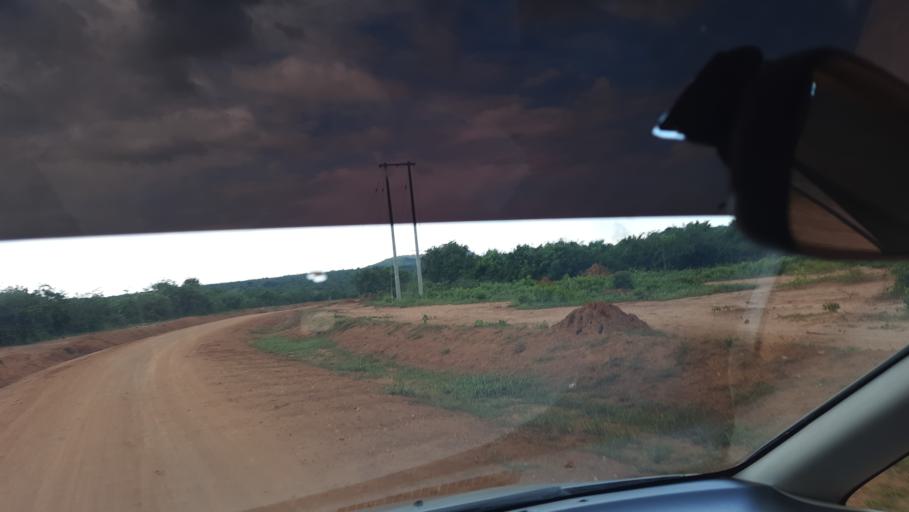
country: UG
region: Central Region
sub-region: Nakasongola District
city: Nakasongola
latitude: 1.3743
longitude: 32.4846
